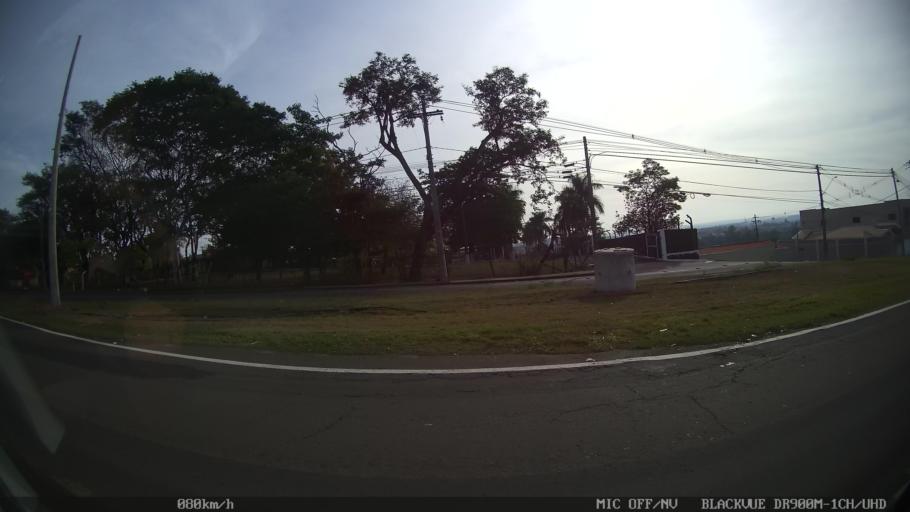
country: BR
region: Sao Paulo
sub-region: Piracicaba
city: Piracicaba
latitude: -22.6811
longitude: -47.6964
